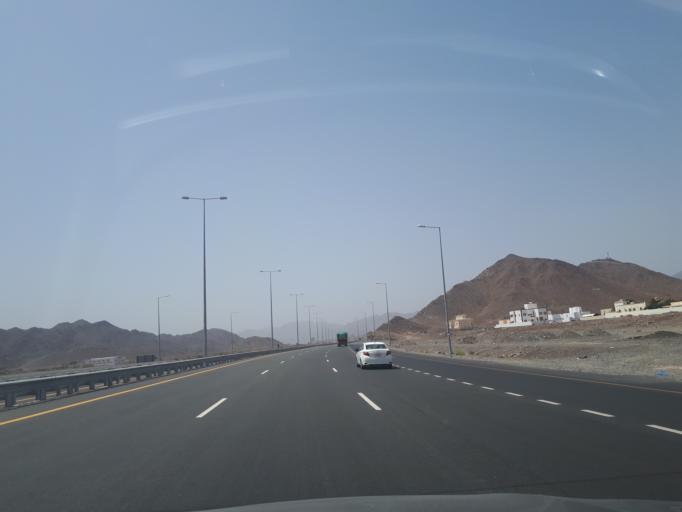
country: OM
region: Muhafazat ad Dakhiliyah
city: Bidbid
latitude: 23.3257
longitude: 58.1158
